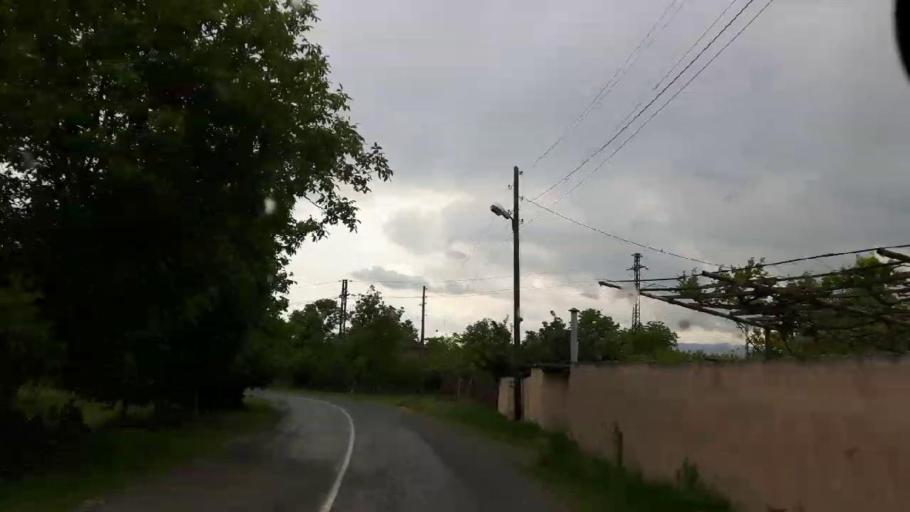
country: GE
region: Shida Kartli
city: Gori
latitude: 41.9626
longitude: 44.2201
